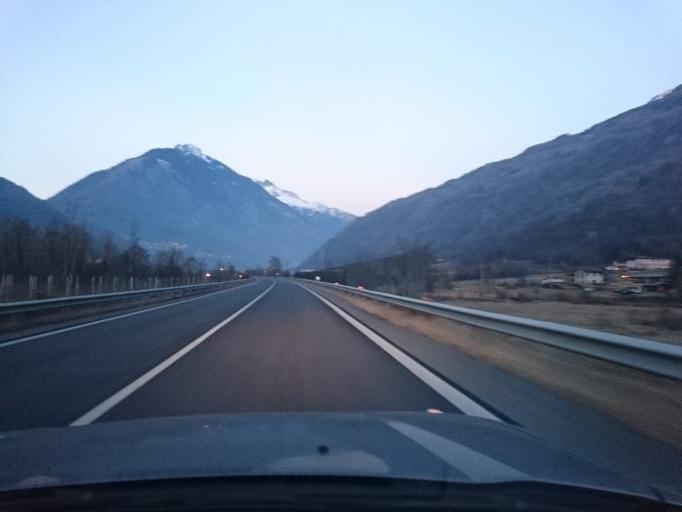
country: IT
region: Lombardy
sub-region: Provincia di Sondrio
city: Mazzo di Valtellina
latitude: 46.2666
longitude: 10.2577
